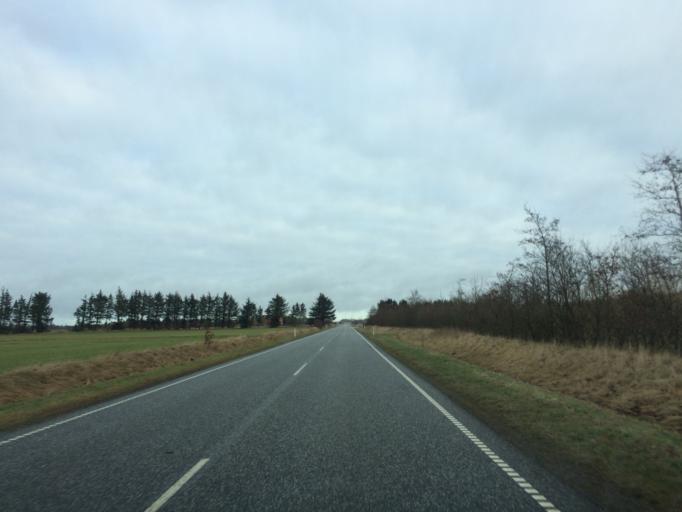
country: DK
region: Central Jutland
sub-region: Struer Kommune
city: Struer
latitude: 56.3913
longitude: 8.4564
